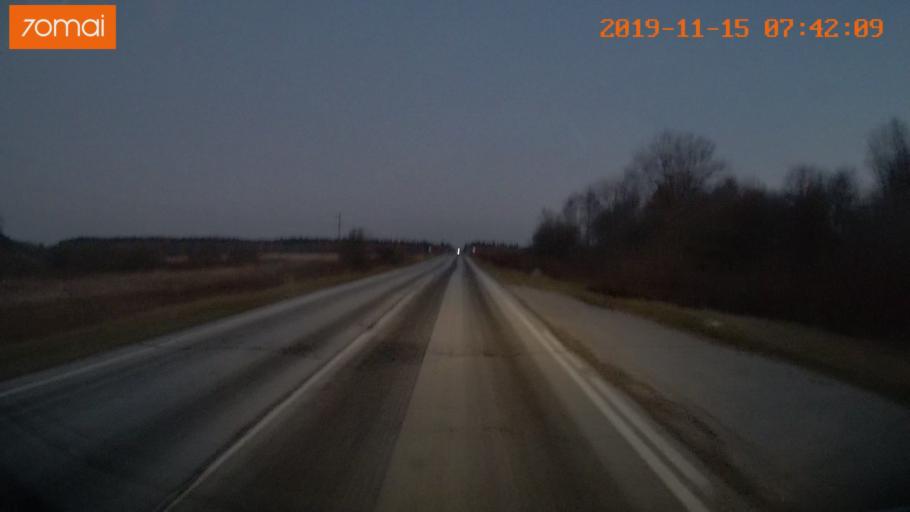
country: RU
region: Vologda
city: Sheksna
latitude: 58.7876
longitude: 38.3483
